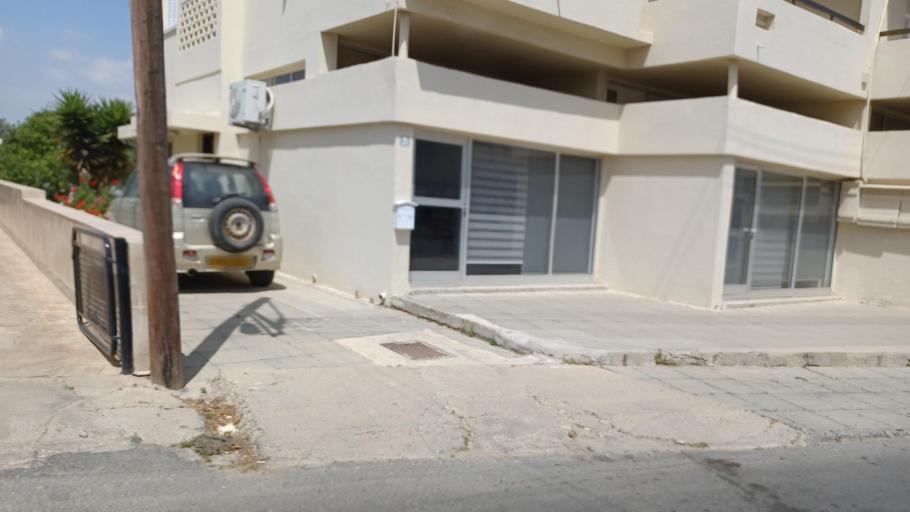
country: CY
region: Ammochostos
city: Paralimni
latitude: 35.0413
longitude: 33.9813
